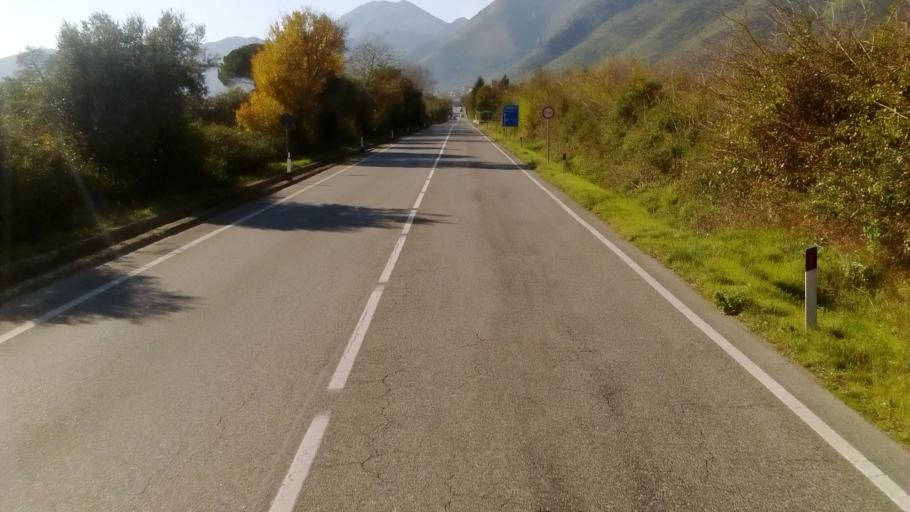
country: IT
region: Molise
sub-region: Provincia di Isernia
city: Pozzilli
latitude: 41.4955
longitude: 14.0772
